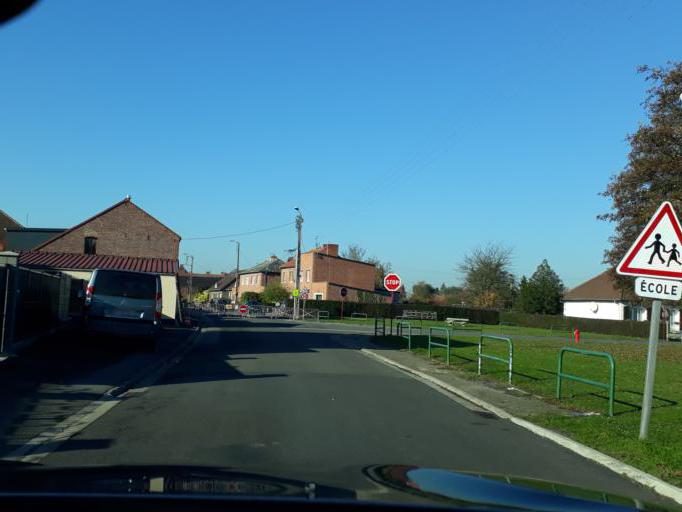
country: FR
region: Nord-Pas-de-Calais
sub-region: Departement du Nord
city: Masny
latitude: 50.3448
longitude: 3.2049
